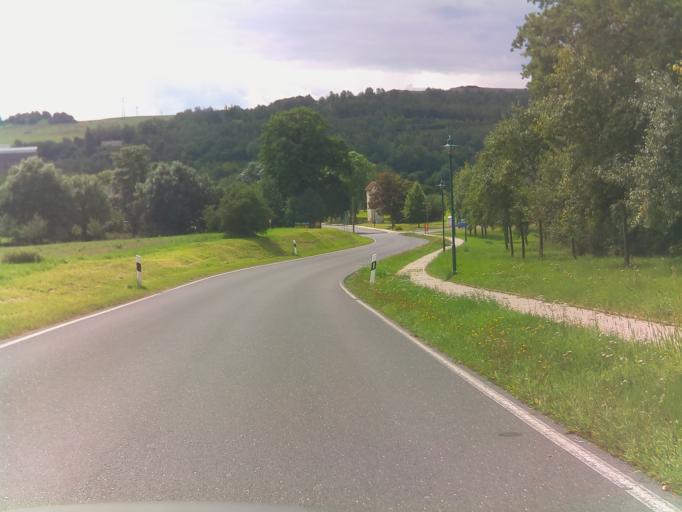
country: DE
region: Thuringia
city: Unterwellenborn
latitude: 50.6631
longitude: 11.4235
